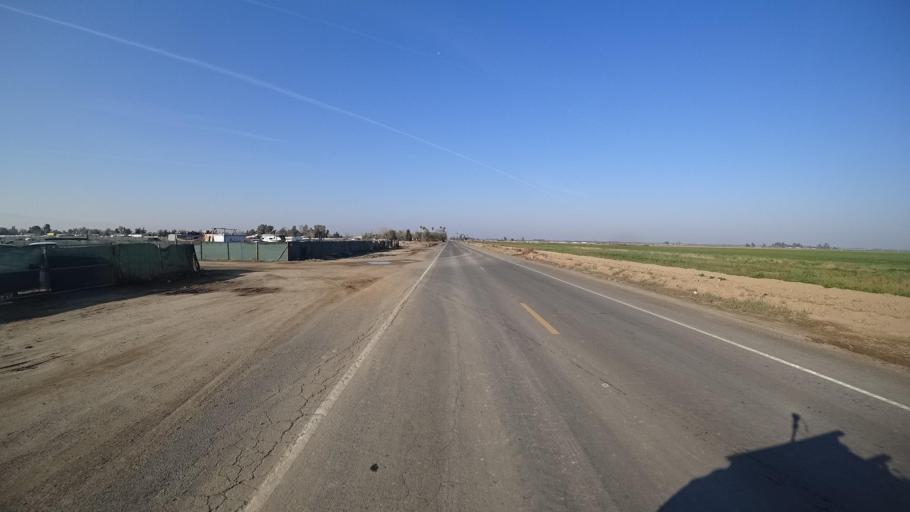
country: US
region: California
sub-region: Kern County
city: Lamont
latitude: 35.2524
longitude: -118.9568
